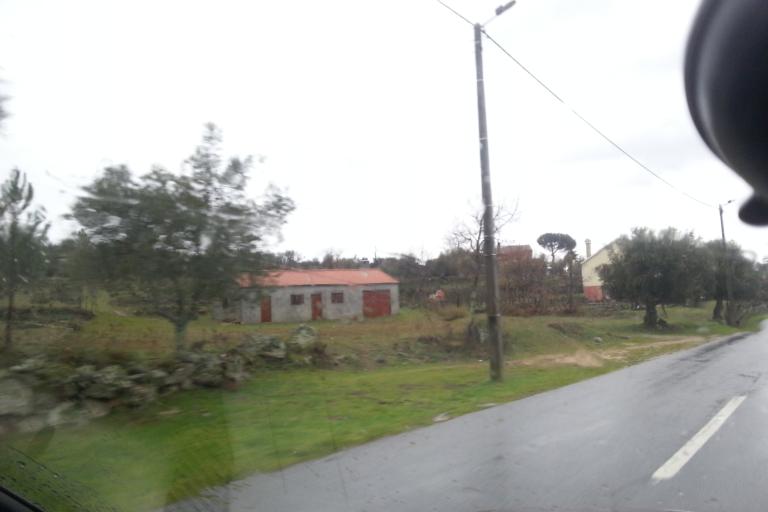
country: PT
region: Guarda
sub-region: Fornos de Algodres
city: Fornos de Algodres
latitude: 40.5832
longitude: -7.5116
